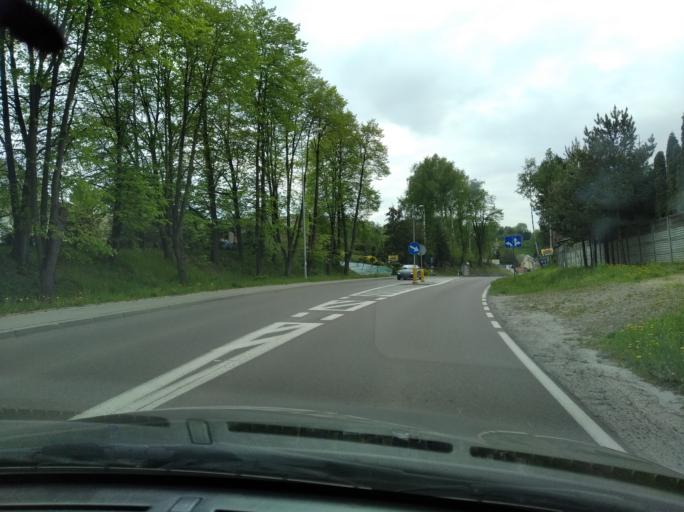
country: PL
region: Lesser Poland Voivodeship
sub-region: Powiat tarnowski
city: Tarnowiec
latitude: 49.9692
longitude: 20.9947
